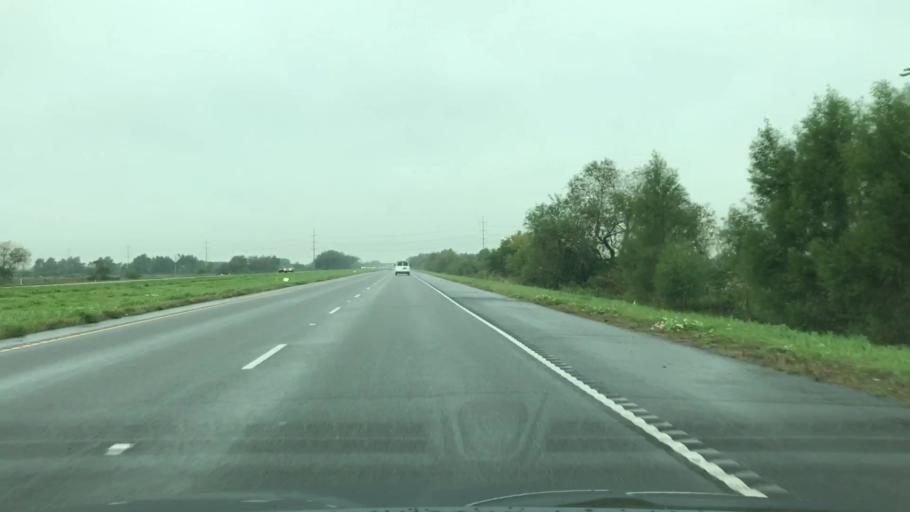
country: US
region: Louisiana
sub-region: Lafourche Parish
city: Raceland
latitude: 29.6902
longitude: -90.6069
